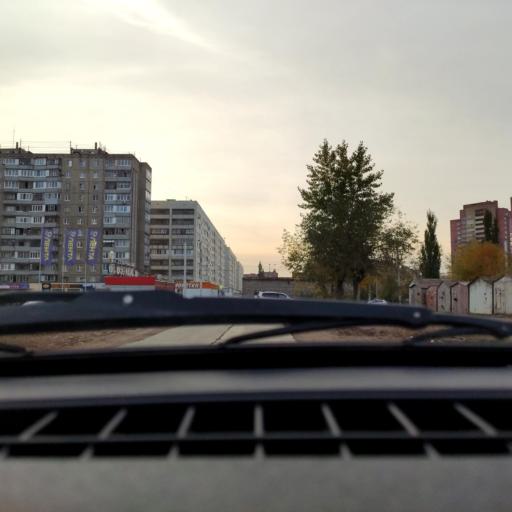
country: RU
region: Bashkortostan
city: Ufa
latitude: 54.7794
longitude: 56.1325
